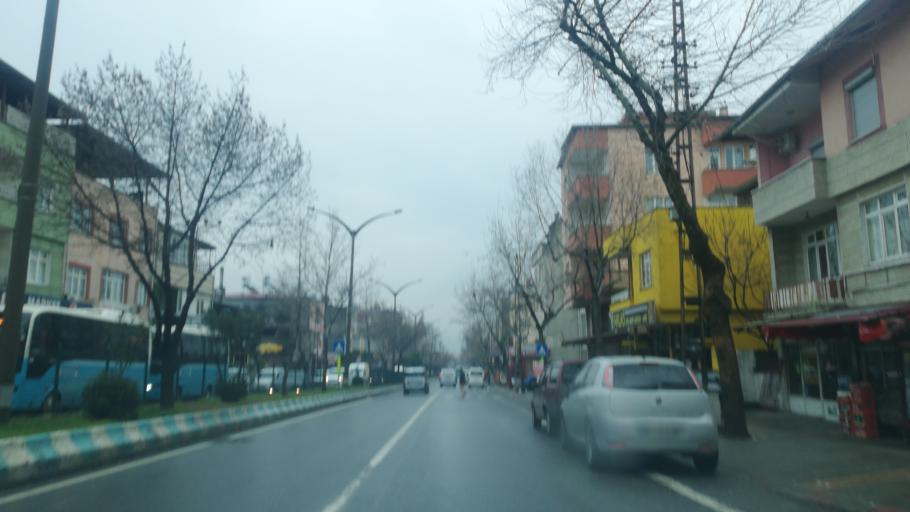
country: TR
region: Kahramanmaras
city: Kahramanmaras
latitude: 37.5687
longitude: 36.9470
